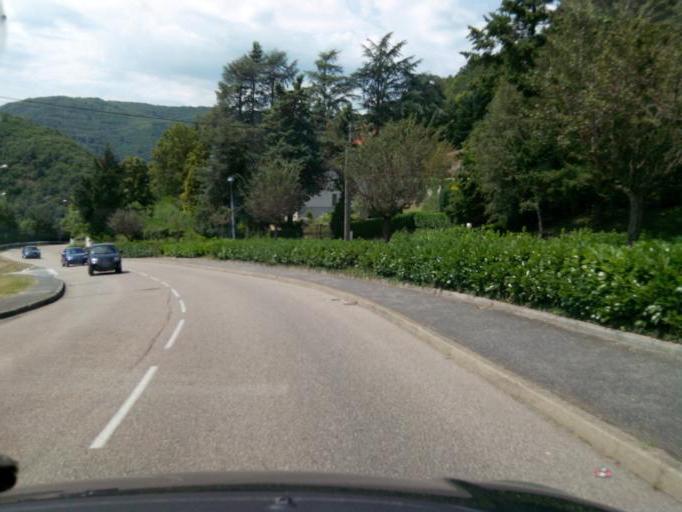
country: FR
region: Rhone-Alpes
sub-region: Departement de la Loire
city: Unieux
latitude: 45.4073
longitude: 4.2595
